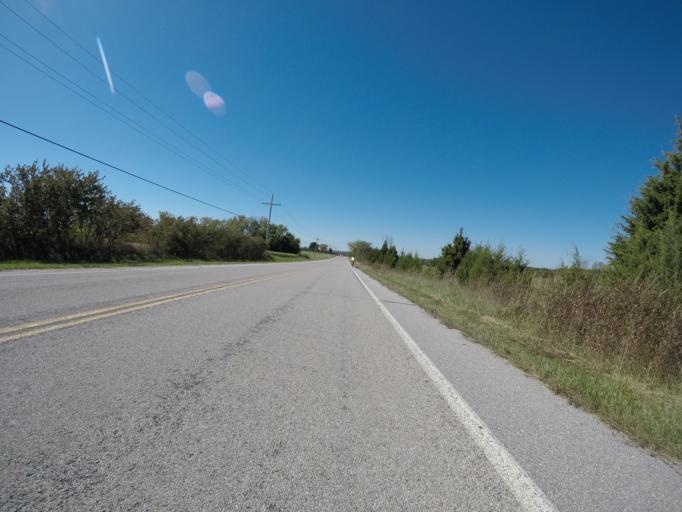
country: US
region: Kansas
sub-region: Douglas County
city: Eudora
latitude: 38.9425
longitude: -95.0435
